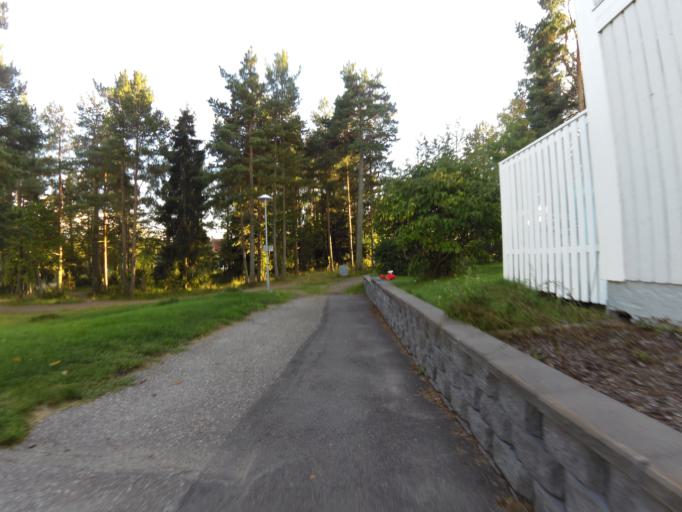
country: SE
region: Gaevleborg
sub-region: Gavle Kommun
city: Gavle
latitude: 60.7272
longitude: 17.1743
